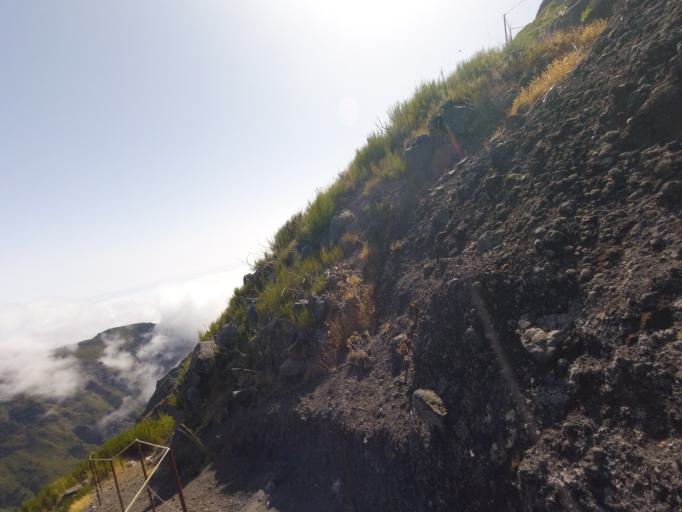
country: PT
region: Madeira
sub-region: Camara de Lobos
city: Curral das Freiras
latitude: 32.7500
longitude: -16.9327
